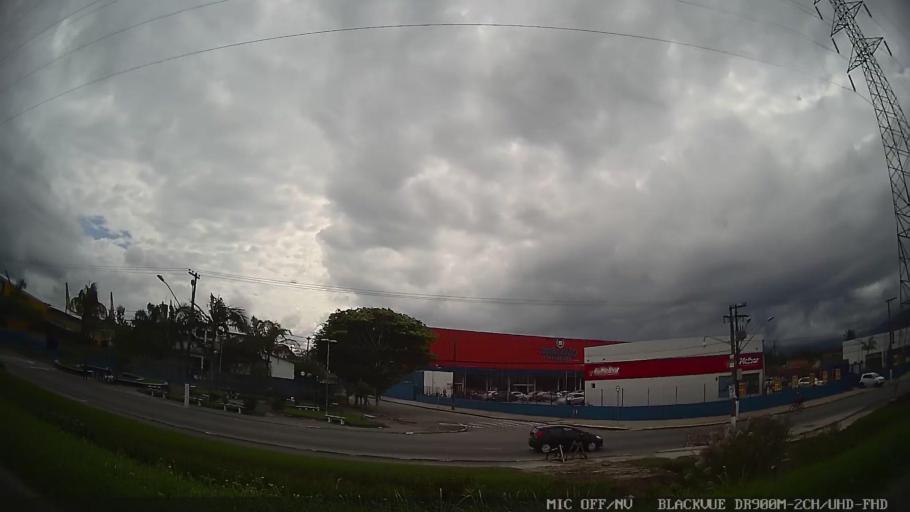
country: BR
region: Sao Paulo
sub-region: Mongagua
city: Mongagua
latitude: -24.1083
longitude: -46.6510
